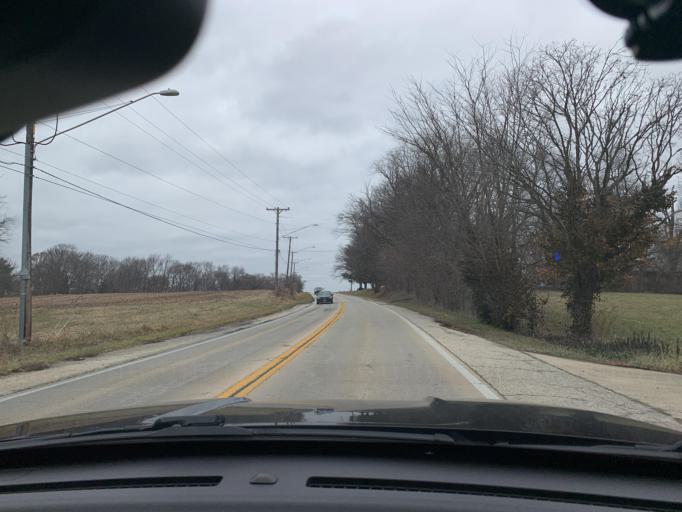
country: US
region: Illinois
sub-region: Sangamon County
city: Jerome
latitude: 39.7305
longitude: -89.6908
